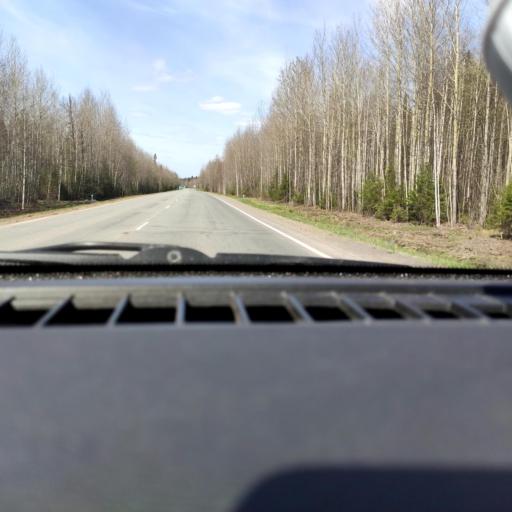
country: RU
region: Perm
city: Polazna
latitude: 58.2845
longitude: 56.1642
